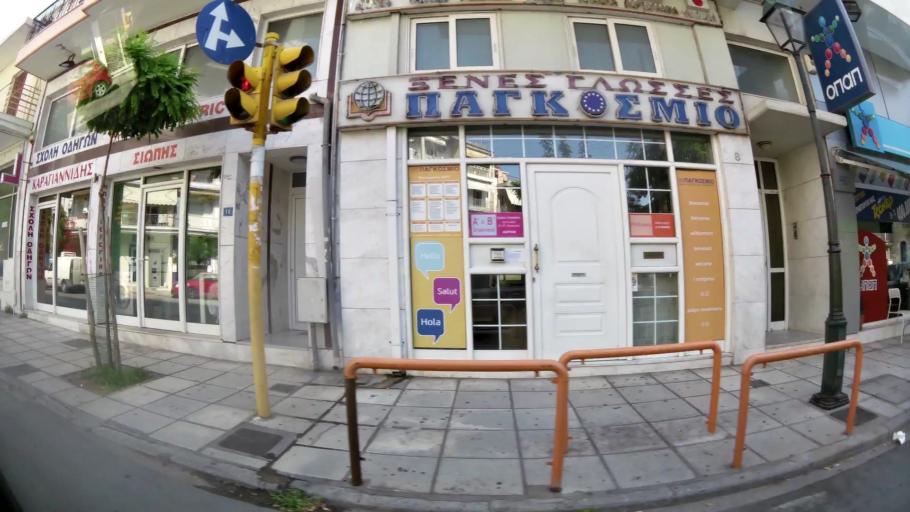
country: GR
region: Central Macedonia
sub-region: Nomos Thessalonikis
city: Thessaloniki
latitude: 40.6463
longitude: 22.9387
